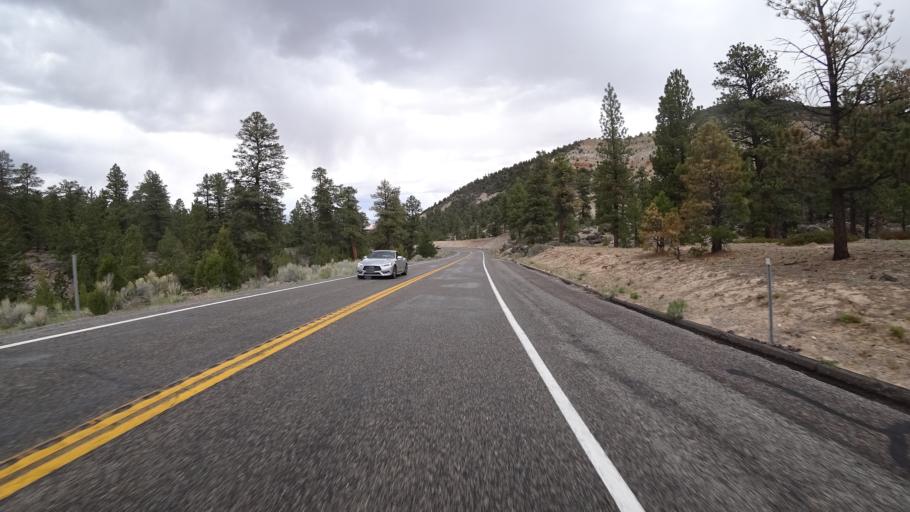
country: US
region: Utah
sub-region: Wayne County
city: Loa
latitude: 38.1818
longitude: -111.3491
